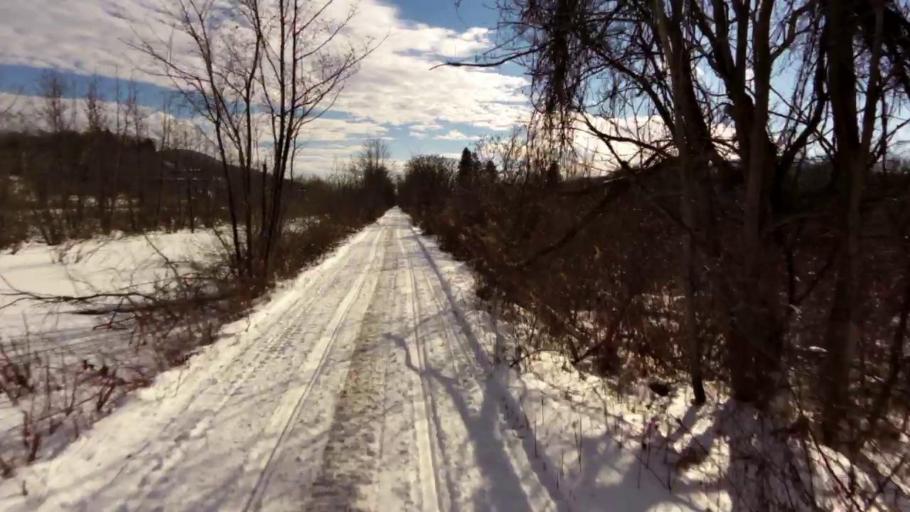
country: US
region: Pennsylvania
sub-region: McKean County
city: Foster Brook
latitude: 42.0391
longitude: -78.6339
